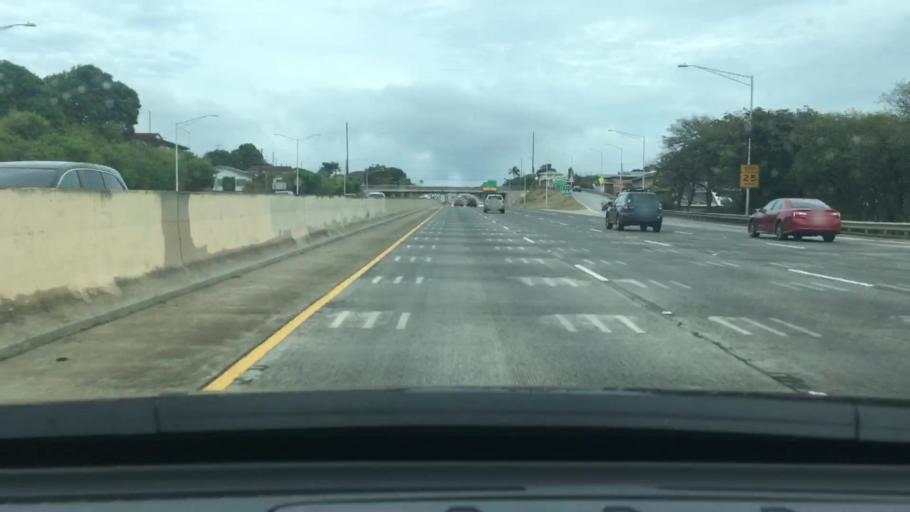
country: US
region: Hawaii
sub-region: Honolulu County
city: Honolulu
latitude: 21.2851
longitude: -157.8096
